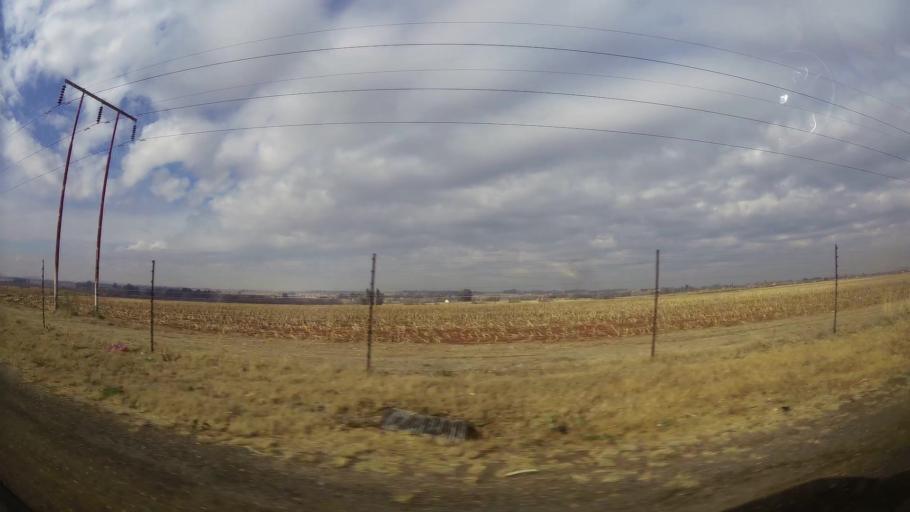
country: ZA
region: Gauteng
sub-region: Sedibeng District Municipality
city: Meyerton
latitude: -26.5576
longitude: 28.0443
